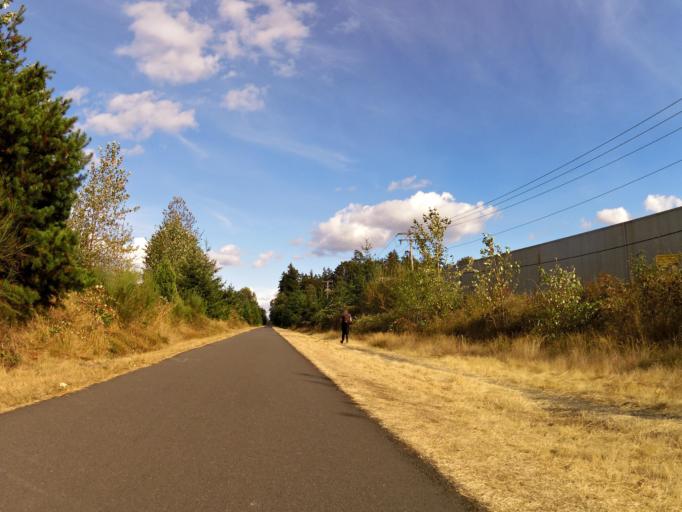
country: US
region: Washington
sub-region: Thurston County
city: Lacey
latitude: 47.0399
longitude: -122.8462
